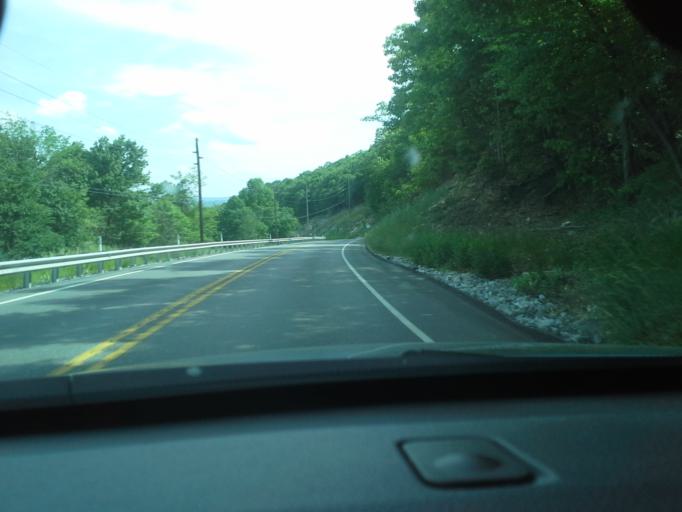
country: US
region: Pennsylvania
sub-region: Fulton County
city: McConnellsburg
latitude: 39.8876
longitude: -77.9658
